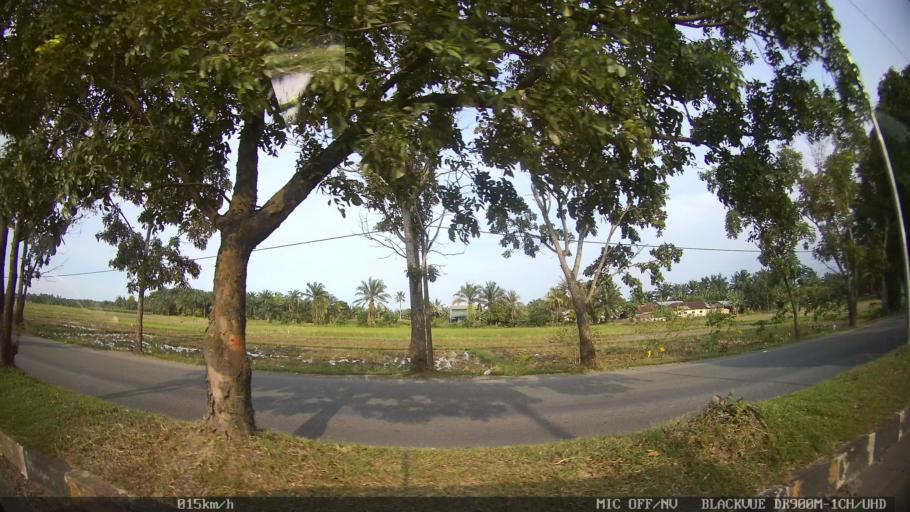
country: ID
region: North Sumatra
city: Binjai
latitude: 3.6174
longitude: 98.5345
